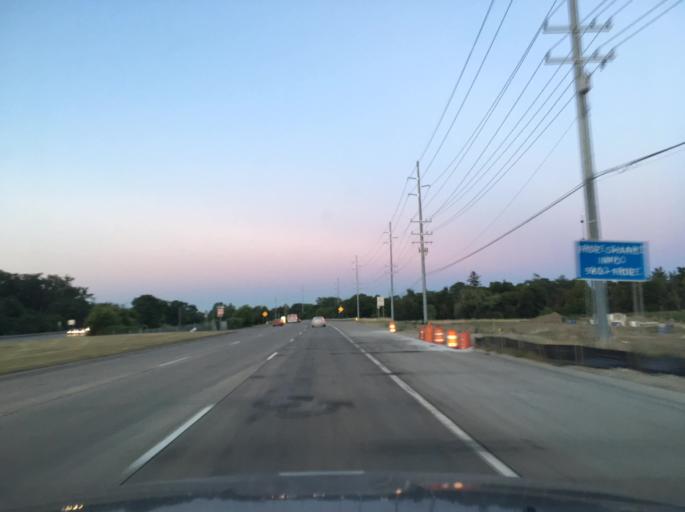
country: US
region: Michigan
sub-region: Macomb County
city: Mount Clemens
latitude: 42.6284
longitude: -82.8926
